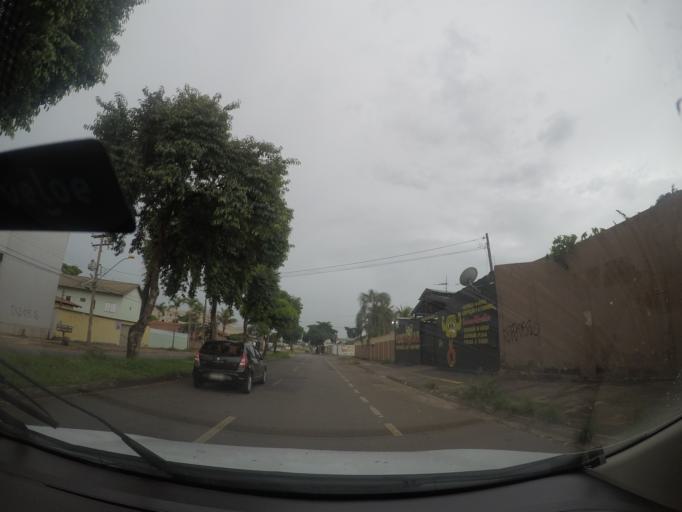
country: BR
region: Goias
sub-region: Goiania
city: Goiania
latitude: -16.6944
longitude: -49.3114
